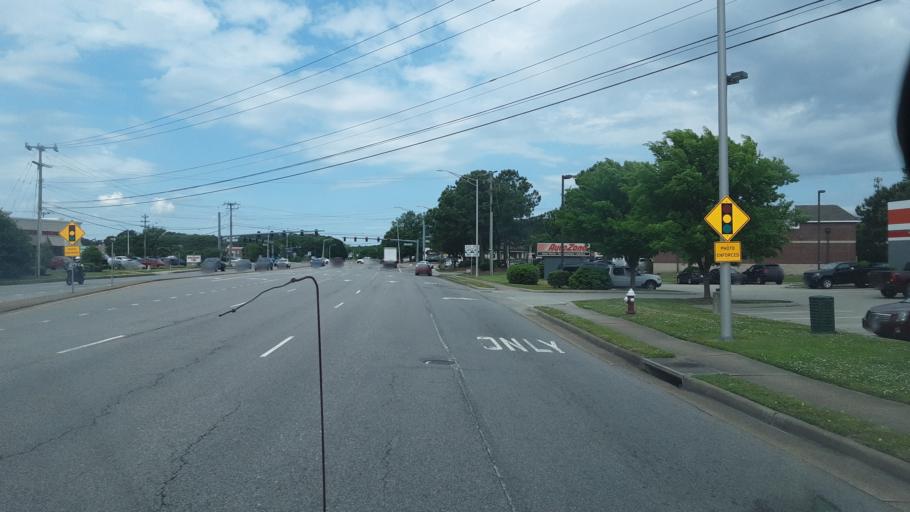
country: US
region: Virginia
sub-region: City of Virginia Beach
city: Virginia Beach
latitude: 36.7861
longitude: -75.9972
